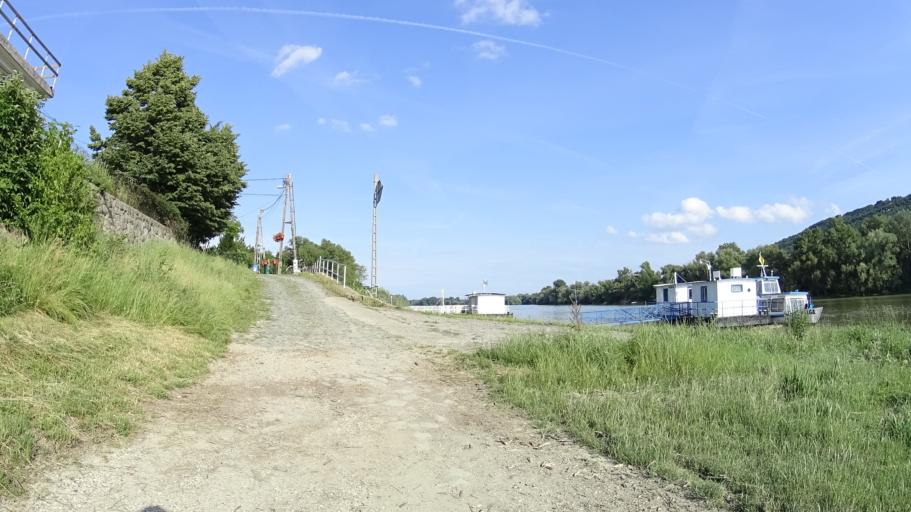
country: HU
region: Pest
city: Veroce
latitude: 47.8061
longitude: 19.0093
